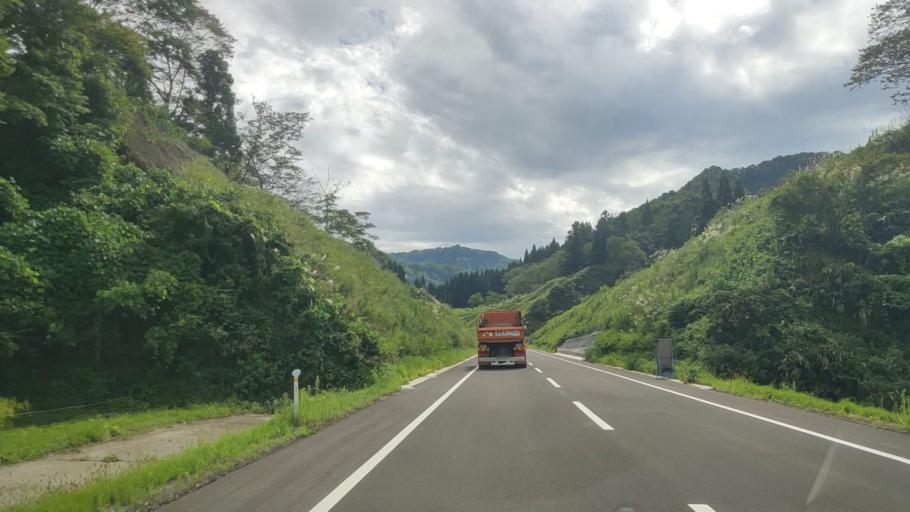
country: JP
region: Niigata
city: Arai
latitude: 36.9483
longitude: 138.2841
